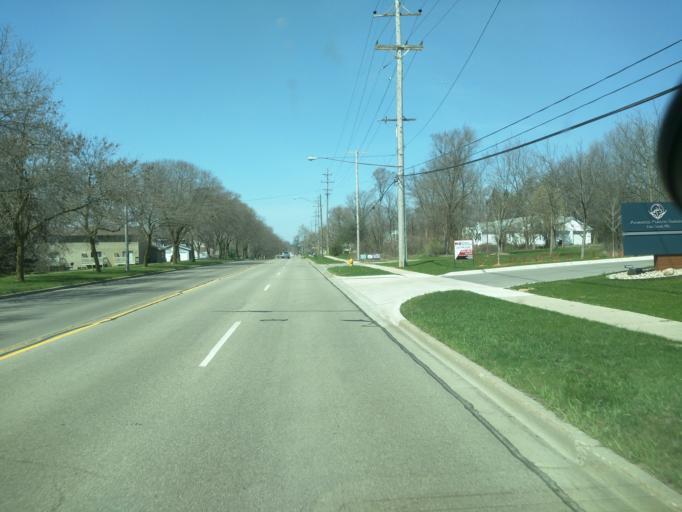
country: US
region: Michigan
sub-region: Kent County
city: East Grand Rapids
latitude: 42.9270
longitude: -85.5728
